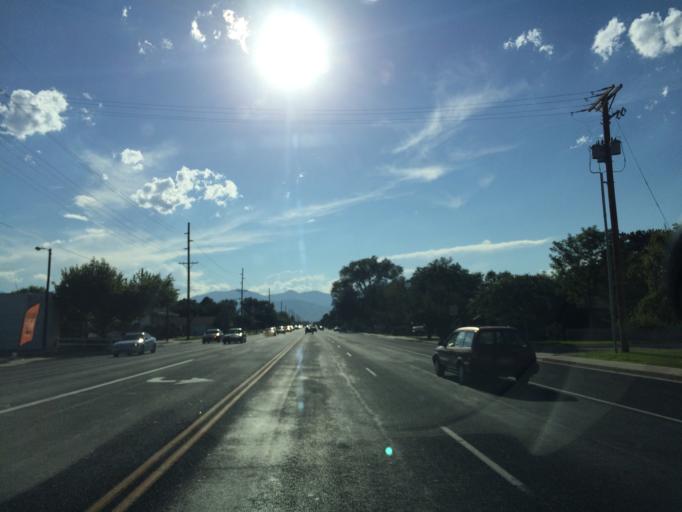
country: US
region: Utah
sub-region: Salt Lake County
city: Taylorsville
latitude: 40.6822
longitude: -111.9678
